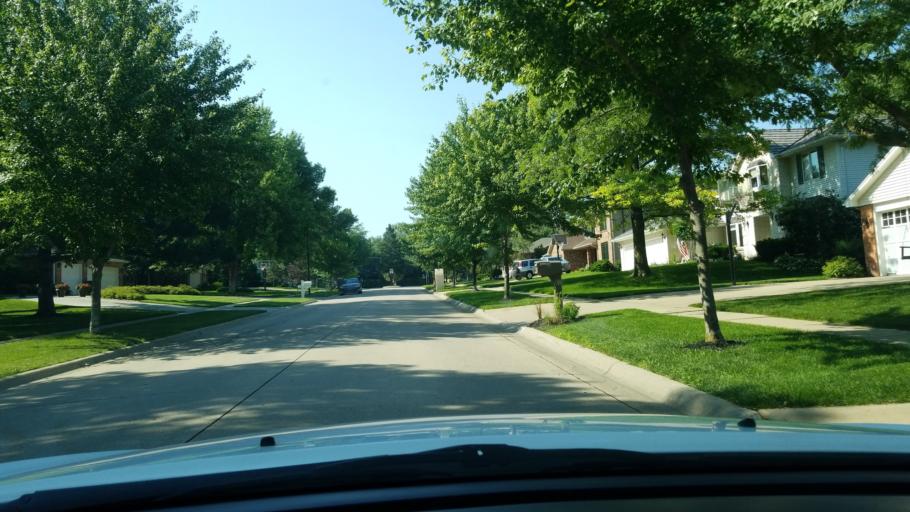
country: US
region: Nebraska
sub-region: Lancaster County
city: Lincoln
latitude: 40.8010
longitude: -96.6318
